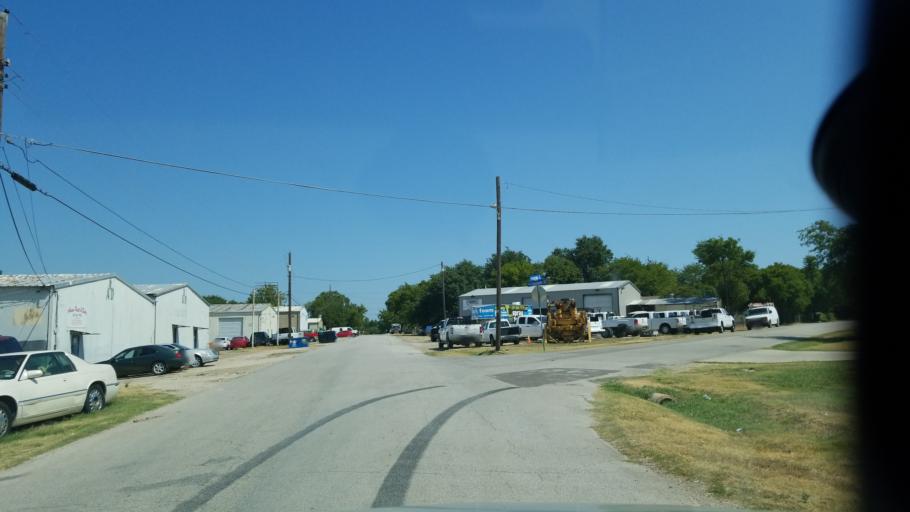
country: US
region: Texas
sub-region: Dallas County
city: Duncanville
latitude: 32.6366
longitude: -96.8990
